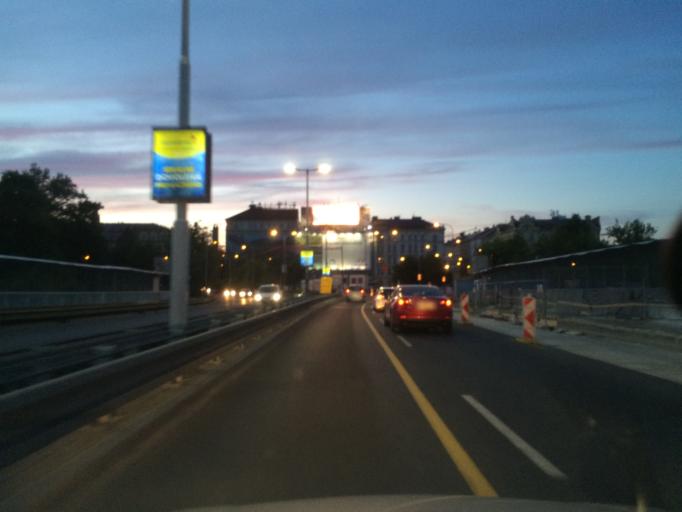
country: CZ
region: Praha
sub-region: Praha 2
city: Vysehrad
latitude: 50.0671
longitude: 14.4302
